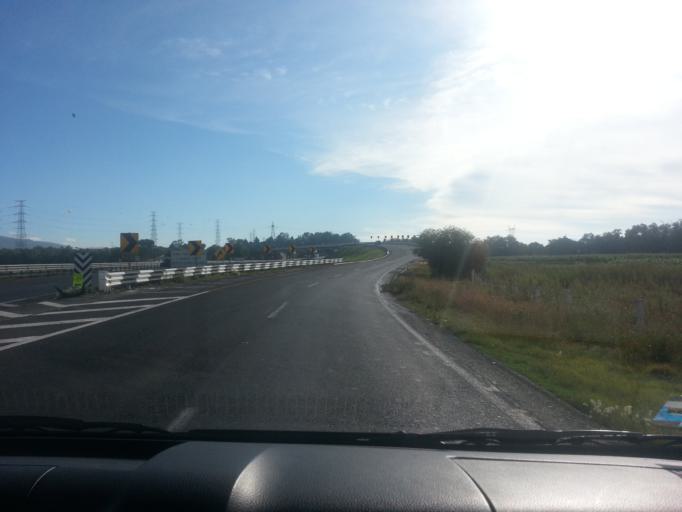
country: MX
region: Morelos
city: Xometla
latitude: 19.6543
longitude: -98.8803
